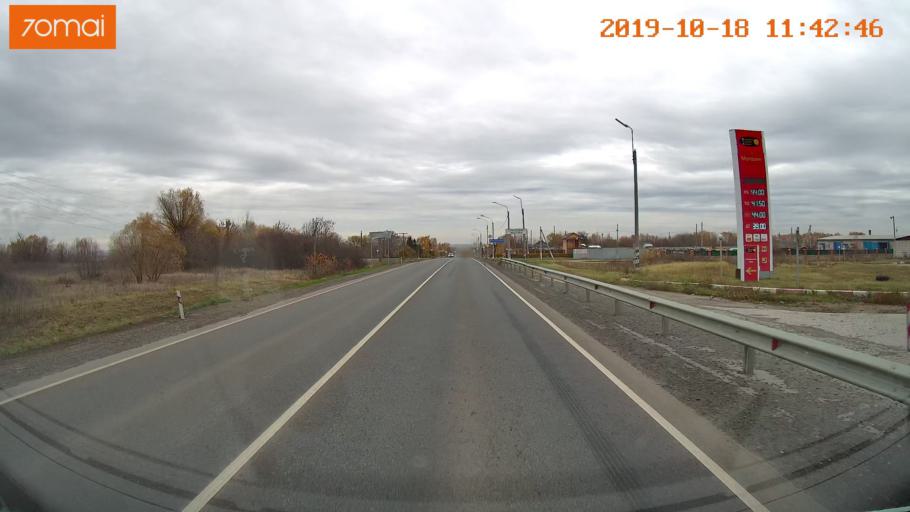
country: RU
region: Rjazan
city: Oktyabr'skiy
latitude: 54.1916
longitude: 38.9340
